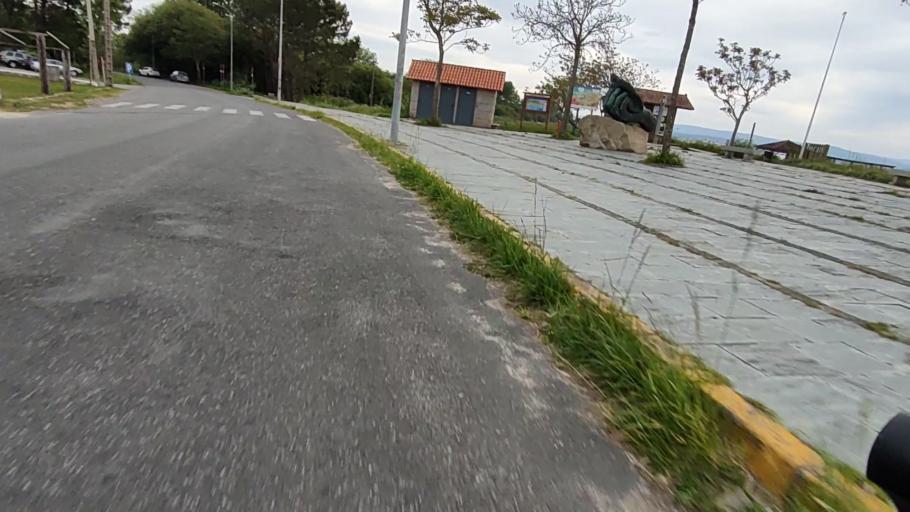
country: ES
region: Galicia
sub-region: Provincia da Coruna
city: Boiro
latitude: 42.6138
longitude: -8.8749
